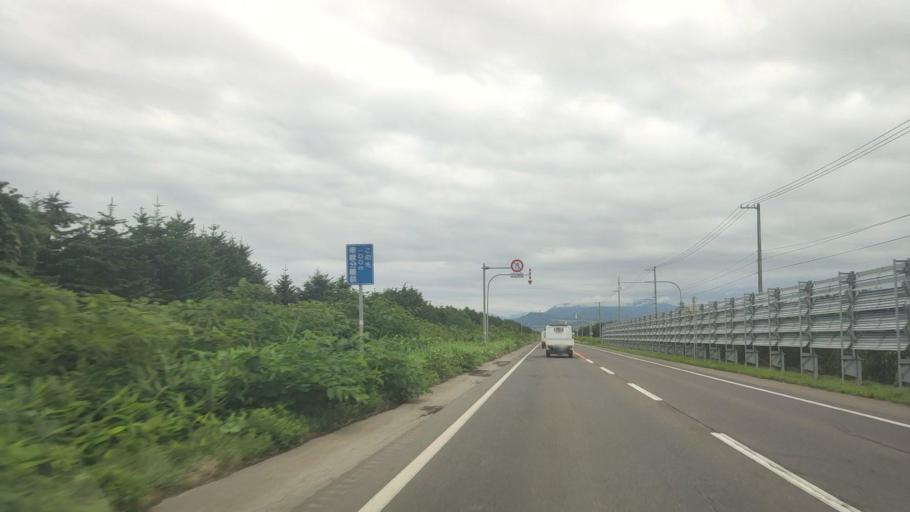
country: JP
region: Hokkaido
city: Nanae
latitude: 42.2964
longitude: 140.2719
